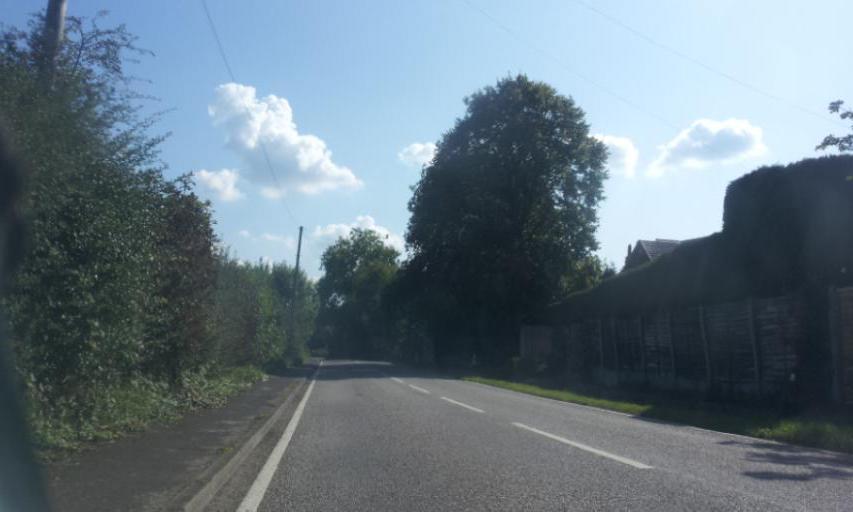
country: GB
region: England
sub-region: Kent
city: East Peckham
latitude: 51.2146
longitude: 0.3942
